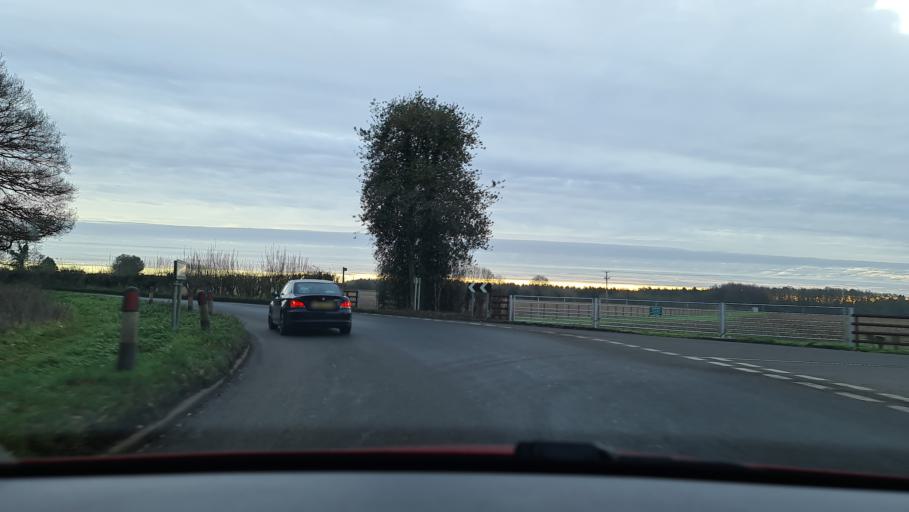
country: GB
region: England
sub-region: Buckinghamshire
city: Amersham
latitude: 51.6895
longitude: -0.6411
